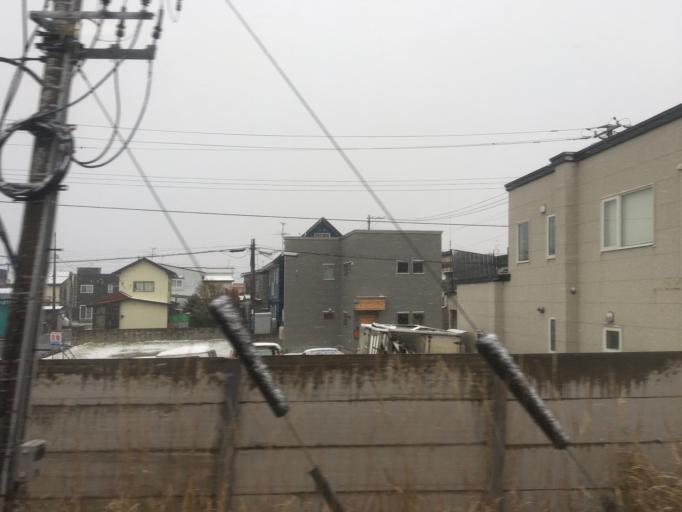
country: JP
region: Aomori
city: Aomori Shi
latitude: 40.8343
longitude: 140.7076
